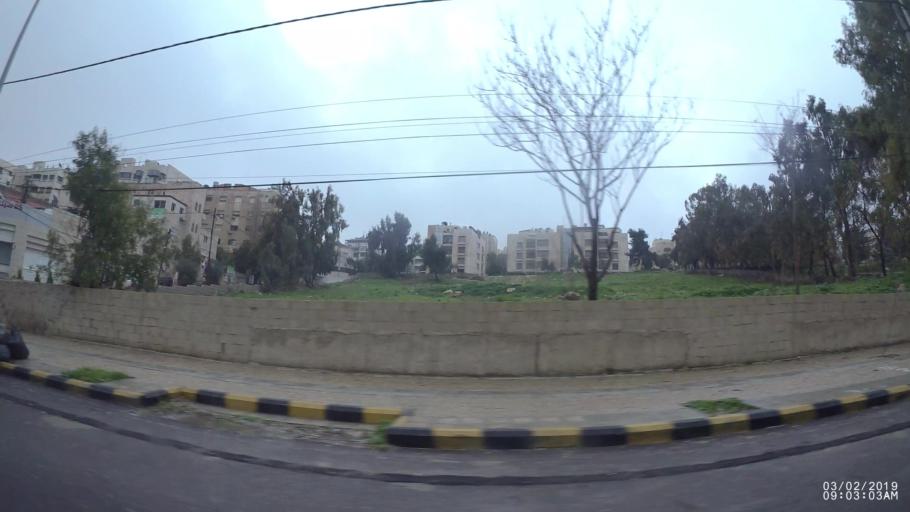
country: JO
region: Amman
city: Amman
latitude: 31.9605
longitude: 35.8926
